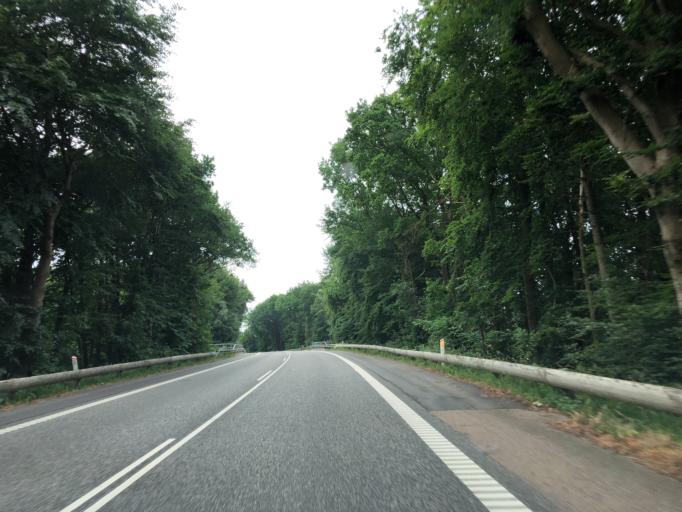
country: DK
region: South Denmark
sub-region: Vejle Kommune
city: Give
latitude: 55.8678
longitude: 9.2411
